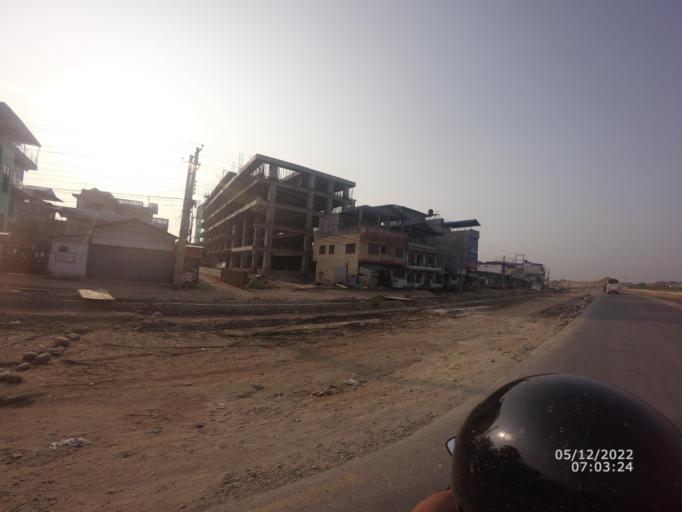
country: NP
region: Central Region
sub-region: Narayani Zone
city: Bharatpur
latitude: 27.6770
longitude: 84.4308
